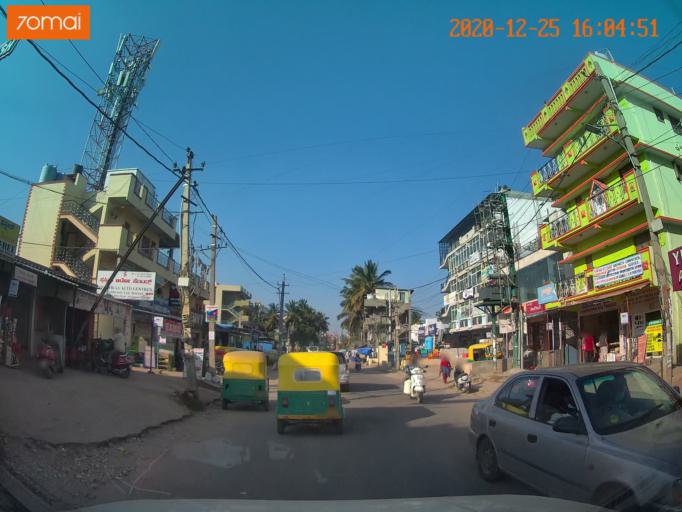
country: IN
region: Karnataka
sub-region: Bangalore Urban
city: Bangalore
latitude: 12.8875
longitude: 77.6256
